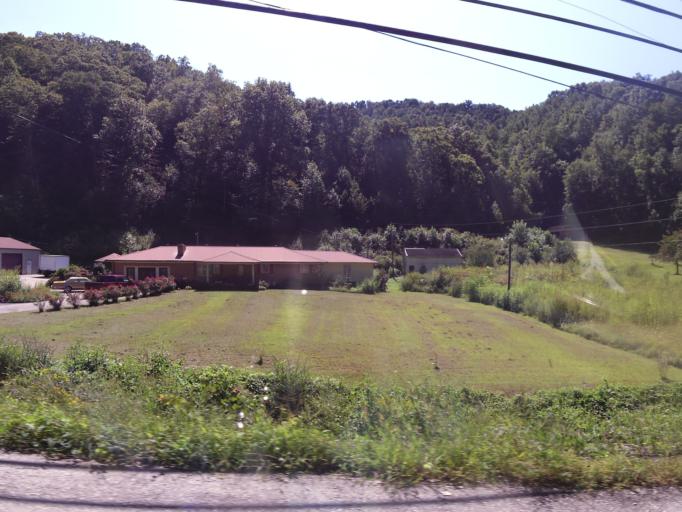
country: US
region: Kentucky
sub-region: Clay County
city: Manchester
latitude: 37.0928
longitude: -83.6696
